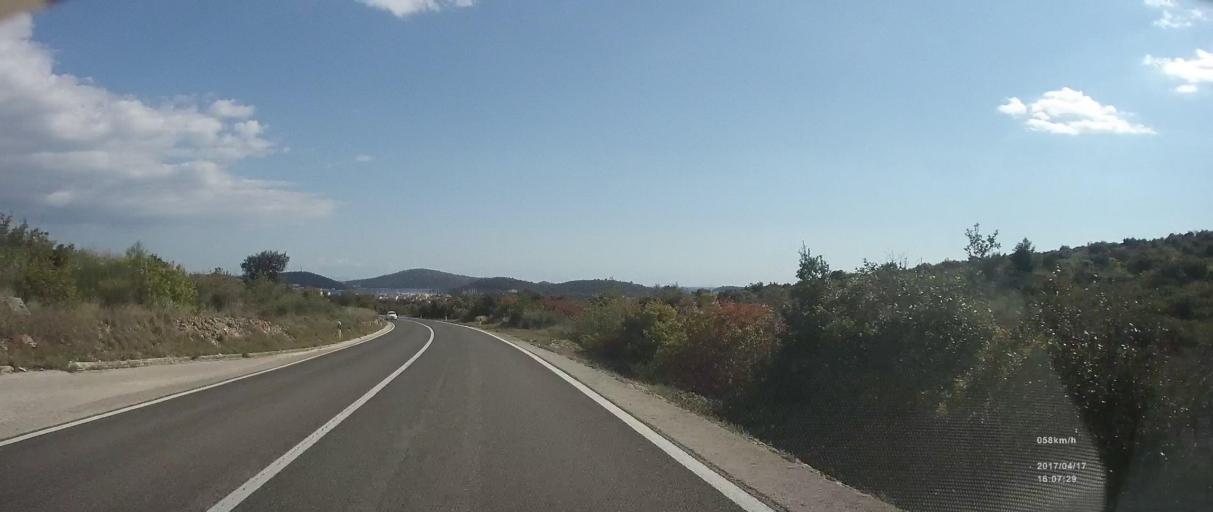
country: HR
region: Sibensko-Kniniska
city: Rogoznica
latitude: 43.5492
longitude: 15.9605
